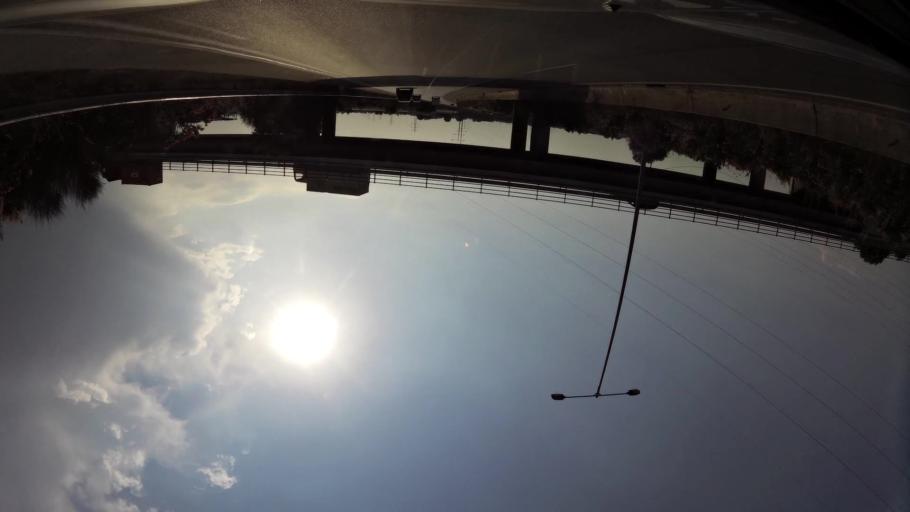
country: GR
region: Central Macedonia
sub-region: Nomos Thessalonikis
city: Diavata
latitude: 40.6971
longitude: 22.8558
